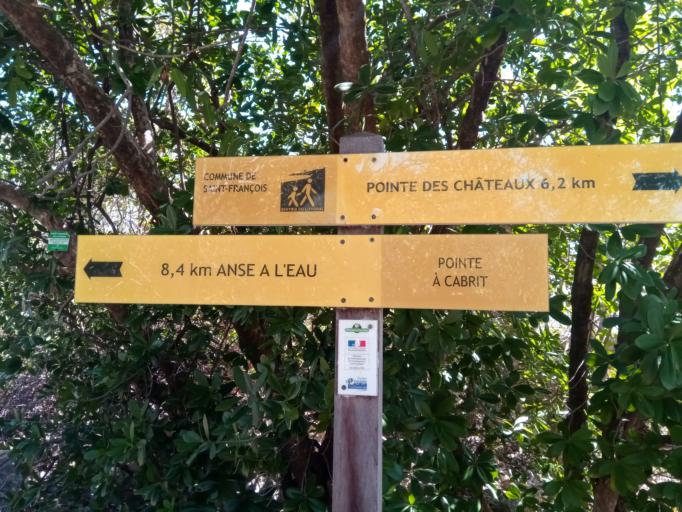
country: GP
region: Guadeloupe
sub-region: Guadeloupe
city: Saint-Francois
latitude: 16.2622
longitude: -61.2191
